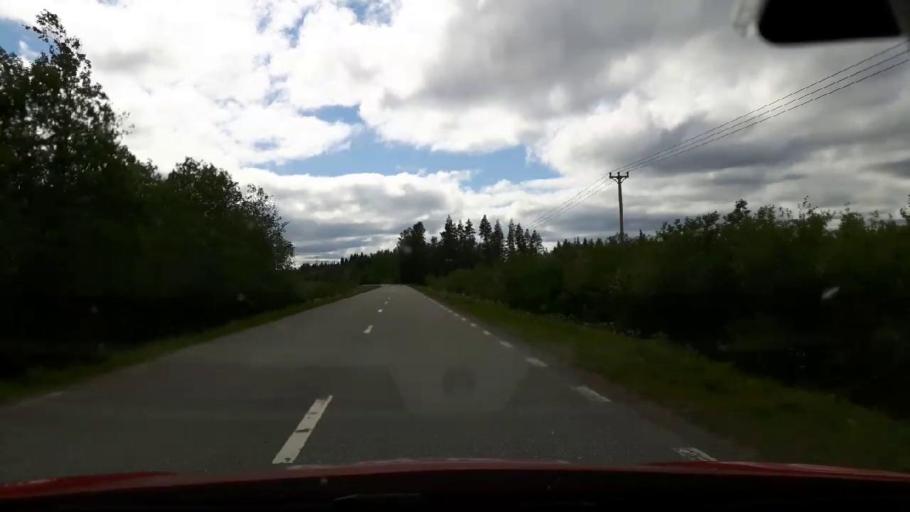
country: SE
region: Jaemtland
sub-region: Ragunda Kommun
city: Hammarstrand
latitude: 63.0174
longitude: 16.1369
